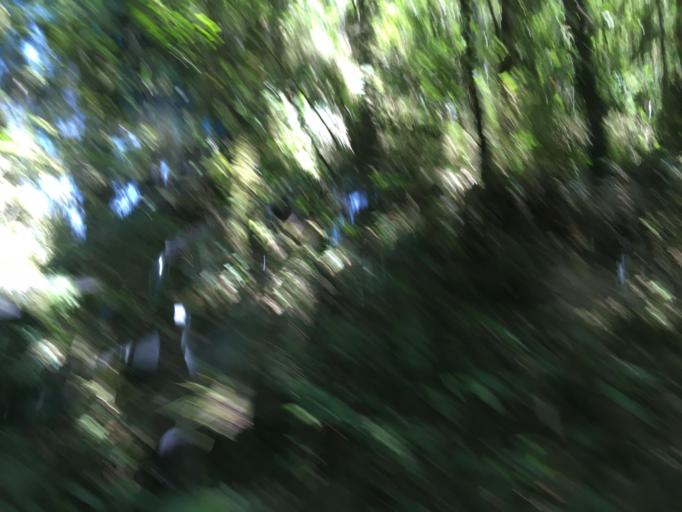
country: TW
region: Taiwan
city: Daxi
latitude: 24.6114
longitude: 121.4606
